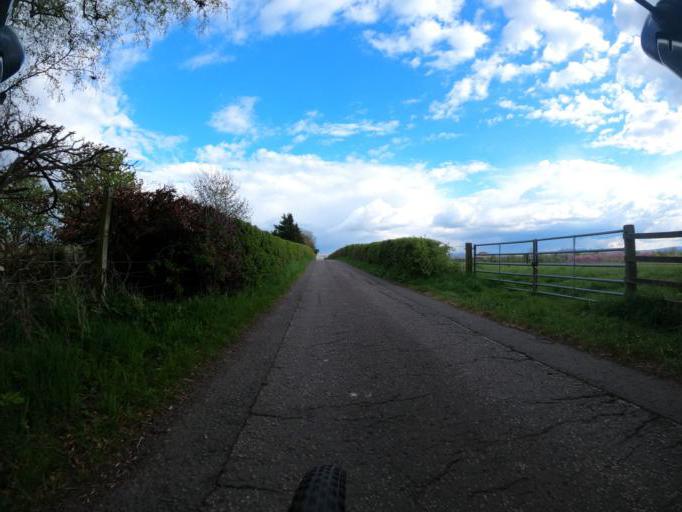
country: GB
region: Scotland
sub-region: Edinburgh
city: Ratho
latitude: 55.9536
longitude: -3.3427
